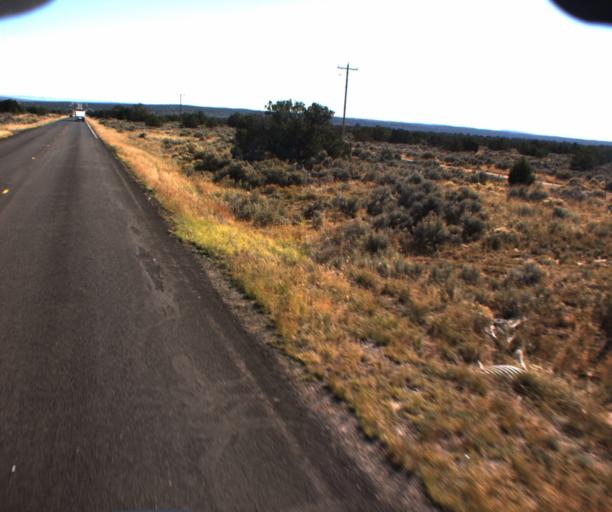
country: US
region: Arizona
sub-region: Apache County
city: Ganado
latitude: 35.5502
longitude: -109.5314
